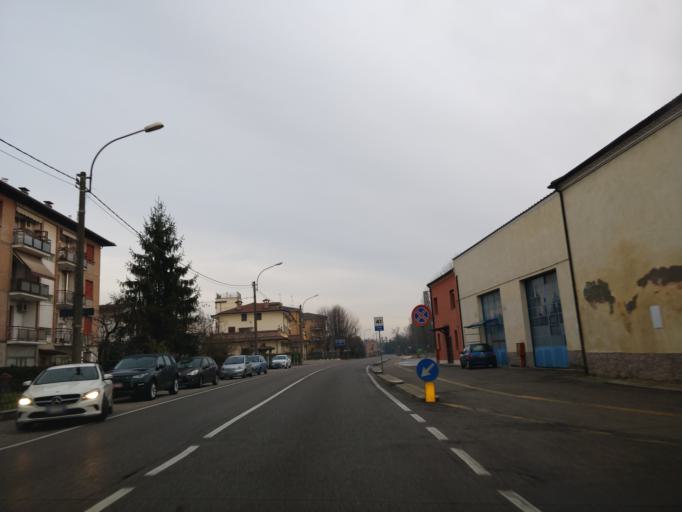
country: IT
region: Emilia-Romagna
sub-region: Provincia di Ferrara
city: Corpo Reno
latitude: 44.7591
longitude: 11.3138
